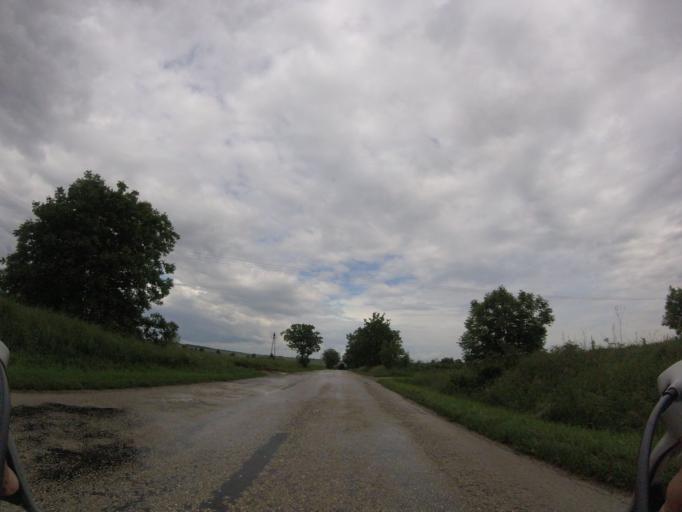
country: HU
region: Baranya
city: Kozarmisleny
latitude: 45.9558
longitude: 18.2309
